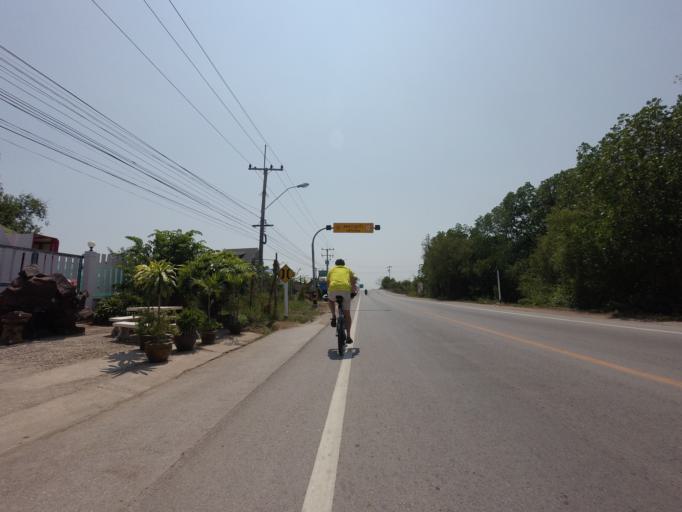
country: TH
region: Samut Sakhon
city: Samut Sakhon
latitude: 13.5144
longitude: 100.3896
